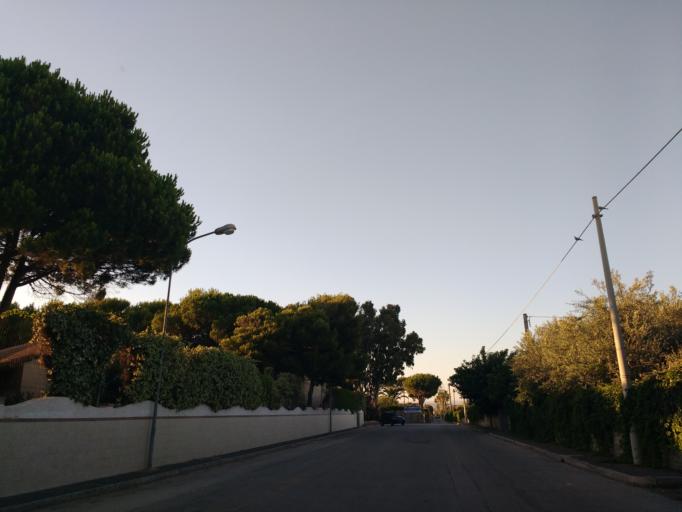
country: IT
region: Sicily
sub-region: Ragusa
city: Ispica
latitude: 36.7243
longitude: 14.9160
